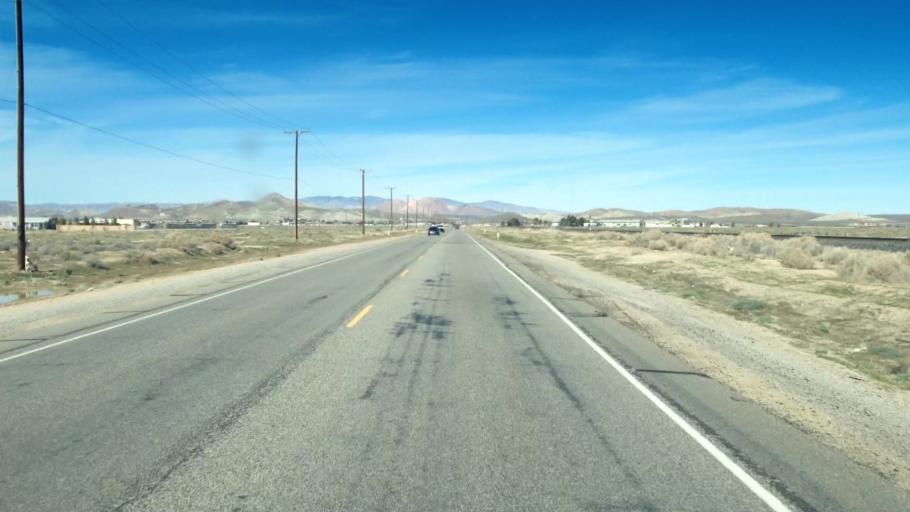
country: US
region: California
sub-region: Kern County
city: Rosamond
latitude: 34.8237
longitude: -118.1566
